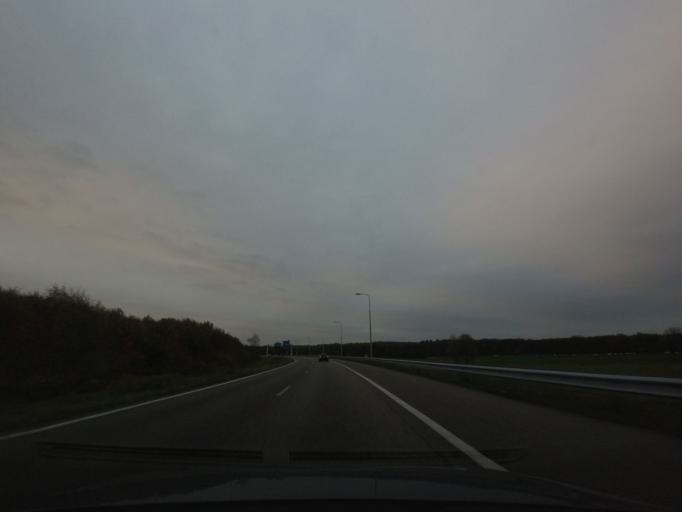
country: NL
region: North Brabant
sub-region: Gemeente Breda
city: Breda
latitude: 51.5582
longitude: 4.8194
